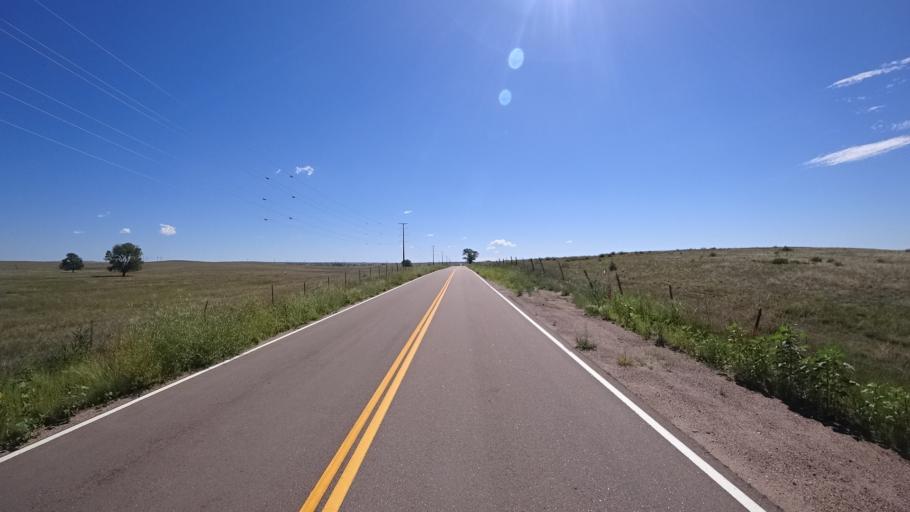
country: US
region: Colorado
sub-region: El Paso County
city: Security-Widefield
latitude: 38.7811
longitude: -104.6471
